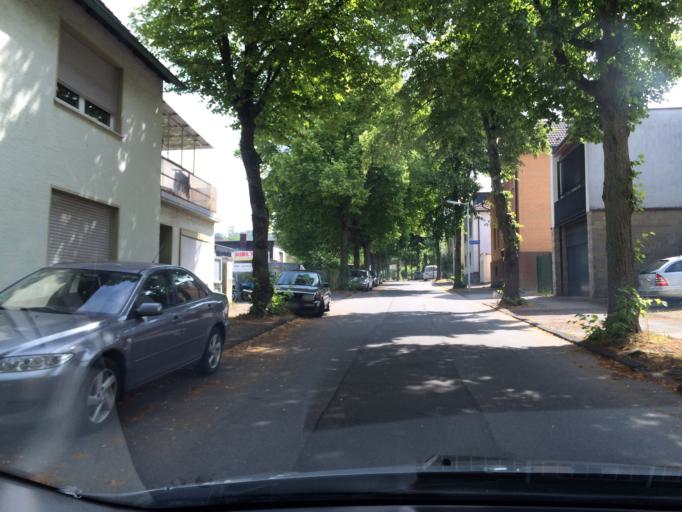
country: DE
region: North Rhine-Westphalia
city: Hemer
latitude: 51.3849
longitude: 7.7740
